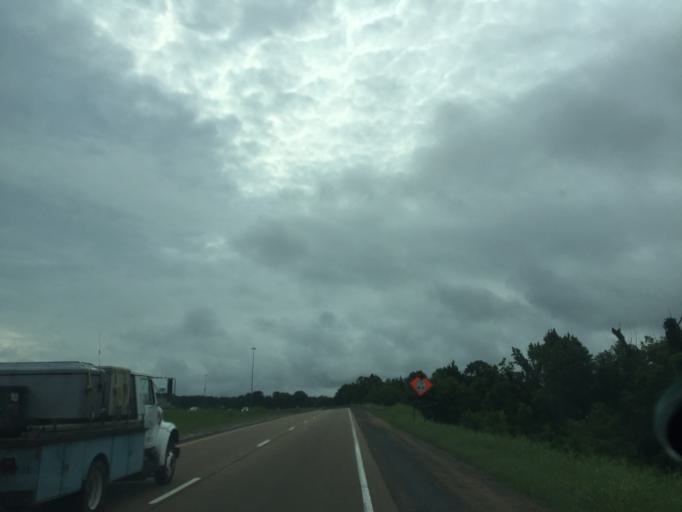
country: US
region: Mississippi
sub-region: Rankin County
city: Brandon
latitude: 32.2790
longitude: -90.0084
